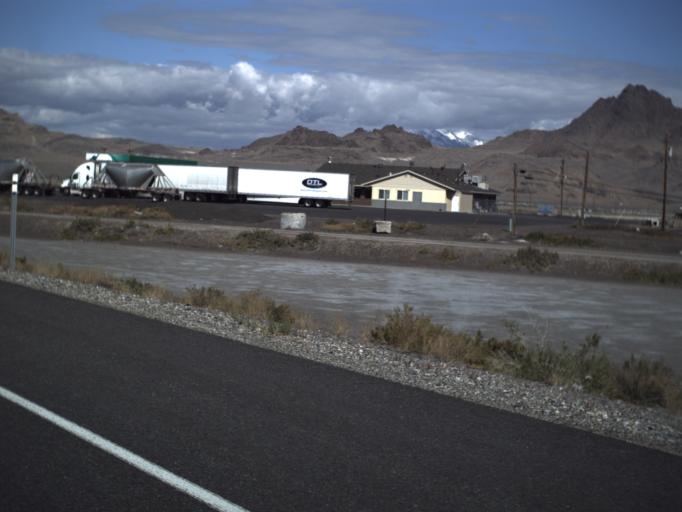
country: US
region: Utah
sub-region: Tooele County
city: Wendover
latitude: 40.7439
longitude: -113.9688
